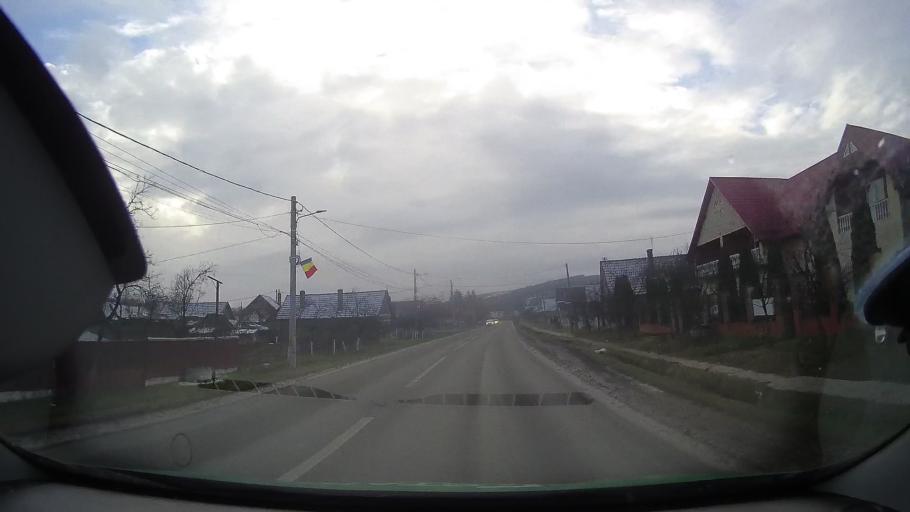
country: RO
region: Mures
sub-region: Comuna Cucerdea
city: Cucerdea
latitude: 46.4078
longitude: 24.2675
